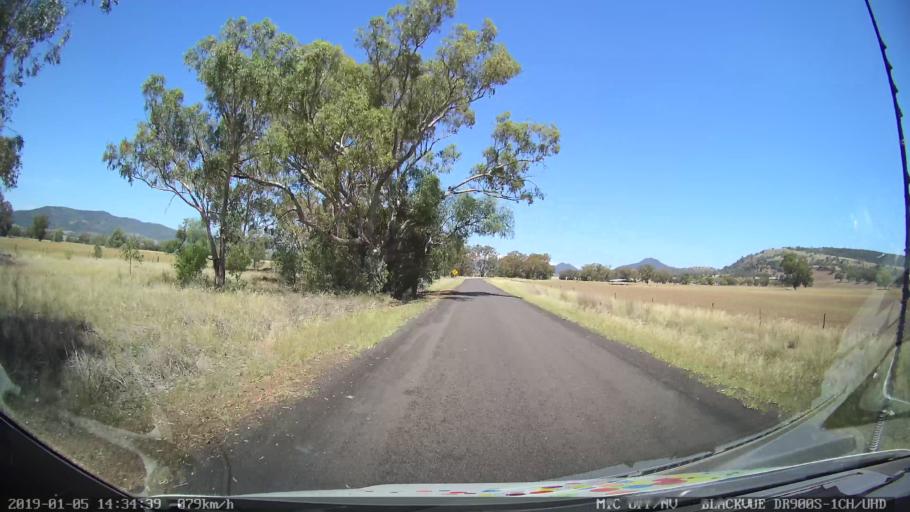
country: AU
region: New South Wales
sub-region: Tamworth Municipality
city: Phillip
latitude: -31.2345
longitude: 150.6440
